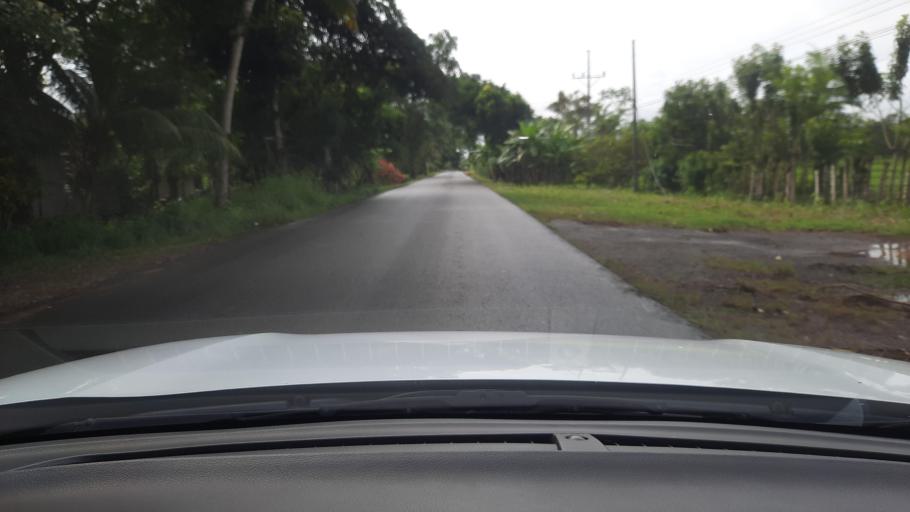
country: CR
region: Alajuela
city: Upala
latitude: 10.9234
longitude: -85.0674
